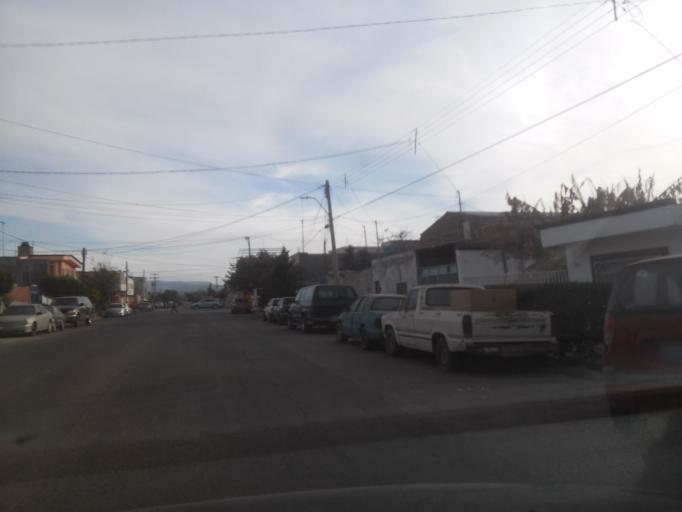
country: MX
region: Durango
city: Victoria de Durango
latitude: 24.0209
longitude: -104.6349
